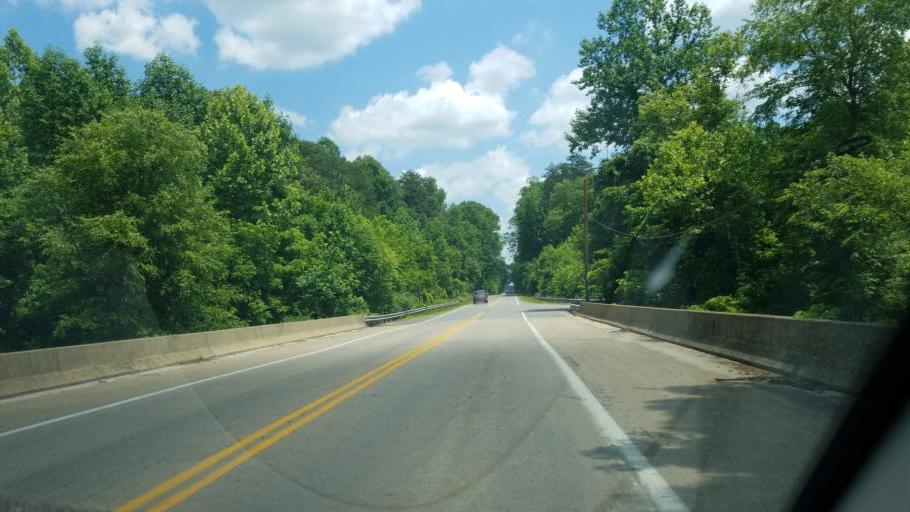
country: US
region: Virginia
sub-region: Cumberland County
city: Cumberland
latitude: 37.4842
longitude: -78.3211
